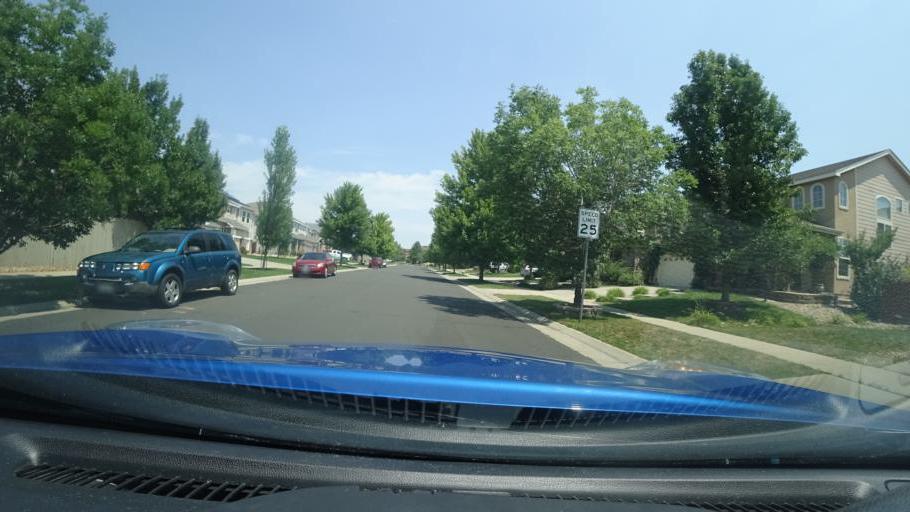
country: US
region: Colorado
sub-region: Adams County
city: Aurora
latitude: 39.6724
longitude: -104.7595
